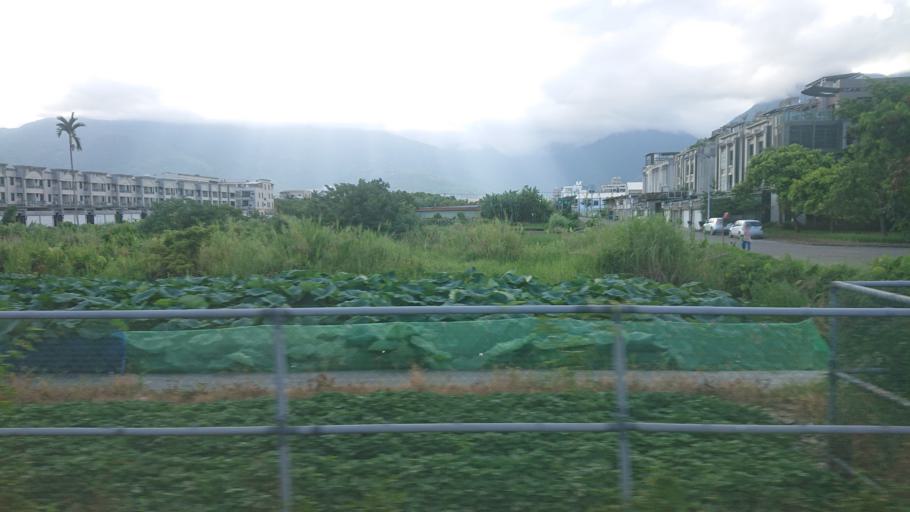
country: TW
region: Taiwan
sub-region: Hualien
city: Hualian
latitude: 23.9781
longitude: 121.5937
